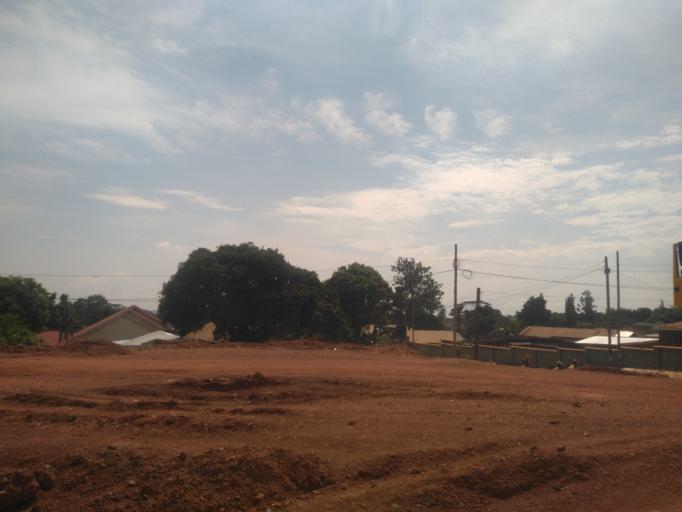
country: UG
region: Central Region
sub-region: Wakiso District
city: Entebbe
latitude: 0.0628
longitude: 32.4729
